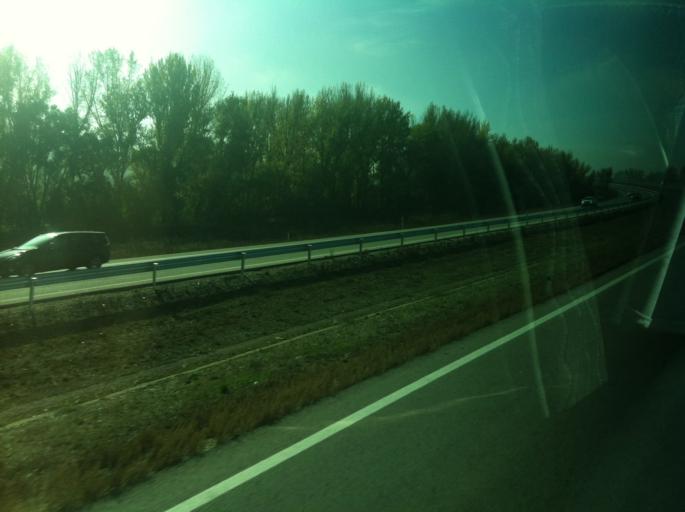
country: ES
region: Castille and Leon
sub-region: Provincia de Burgos
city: Rubena
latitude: 42.3908
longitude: -3.5766
